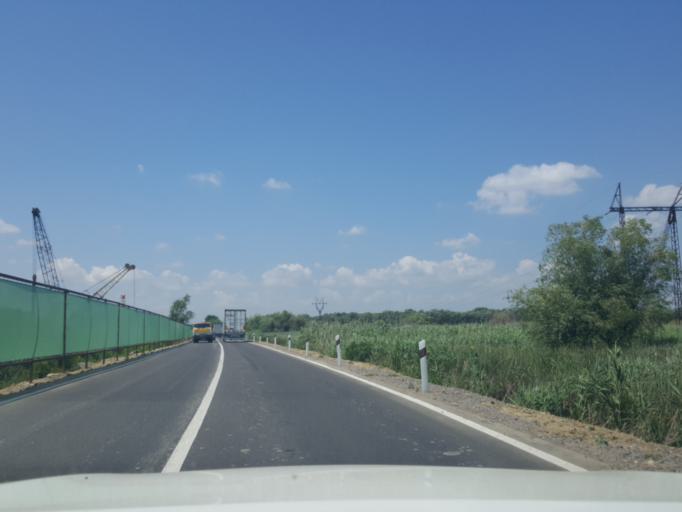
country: UA
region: Odessa
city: Bilyayivka
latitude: 46.4145
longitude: 30.1576
